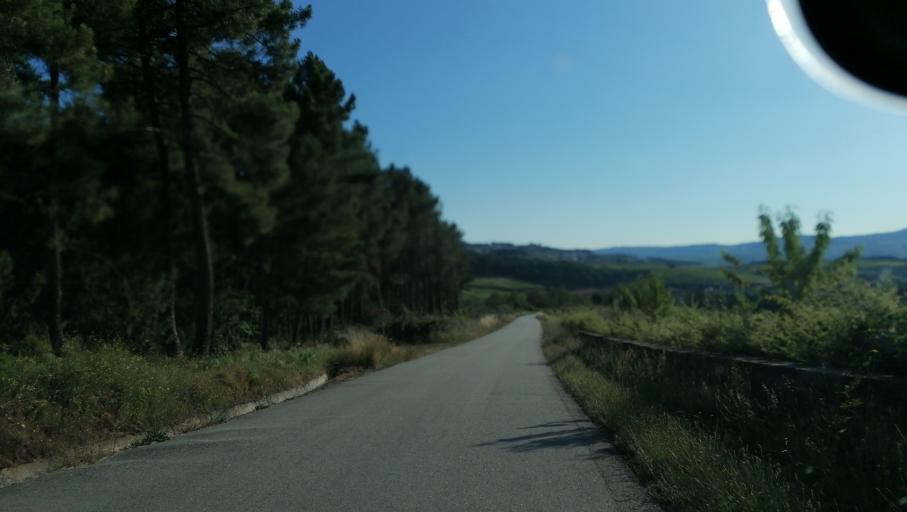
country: PT
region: Vila Real
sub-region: Sabrosa
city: Sabrosa
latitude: 41.2520
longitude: -7.5925
